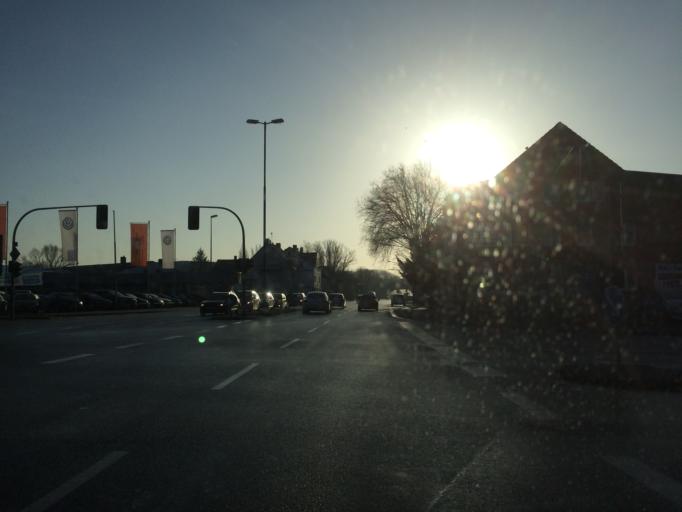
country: DE
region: North Rhine-Westphalia
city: Bochum-Hordel
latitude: 51.5440
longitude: 7.1628
